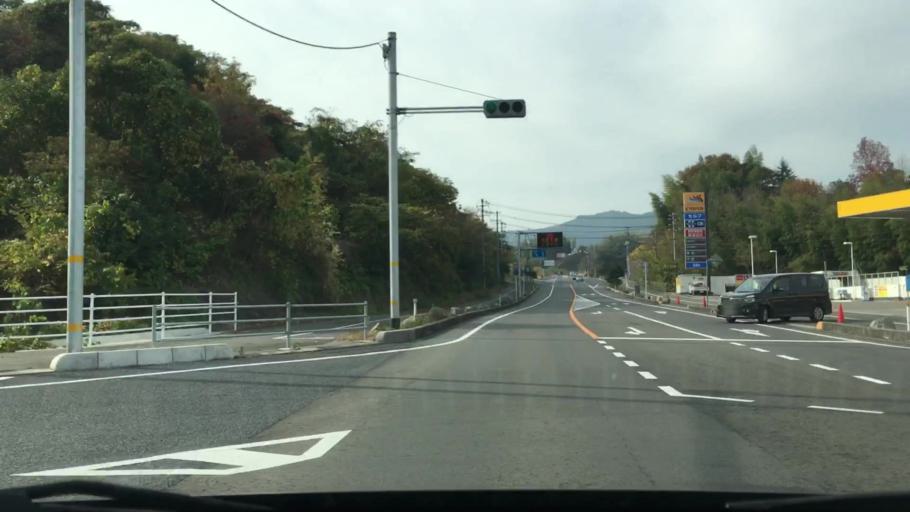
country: JP
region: Yamaguchi
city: Iwakuni
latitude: 34.1535
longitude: 132.1909
